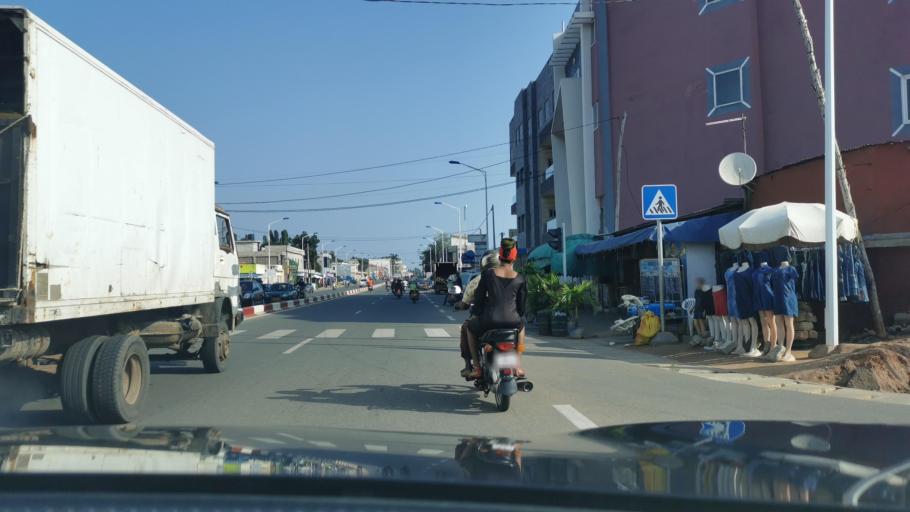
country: TG
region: Maritime
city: Lome
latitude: 6.1715
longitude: 1.2345
